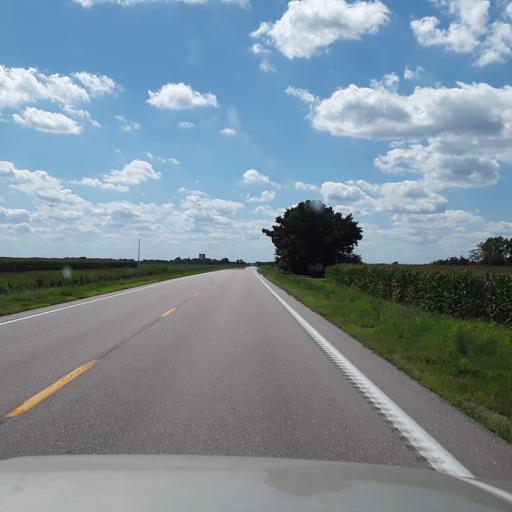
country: US
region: Nebraska
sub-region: Merrick County
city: Central City
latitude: 41.1913
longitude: -98.0747
